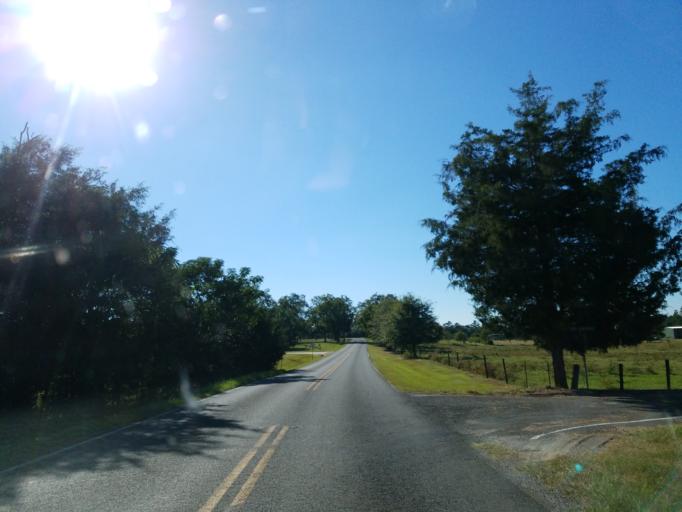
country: US
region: Georgia
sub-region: Dooly County
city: Unadilla
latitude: 32.2525
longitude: -83.7845
